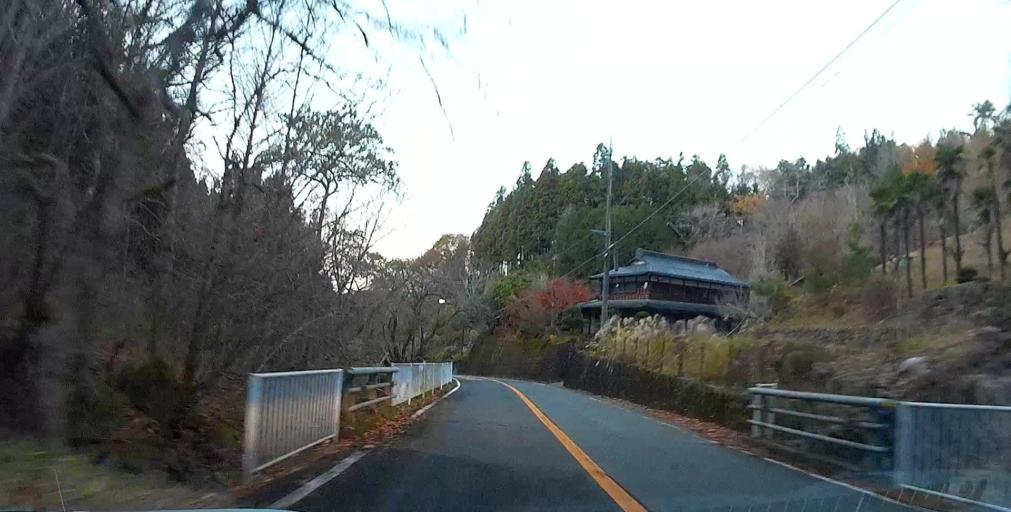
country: JP
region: Yamanashi
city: Uenohara
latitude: 35.5833
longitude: 139.1762
